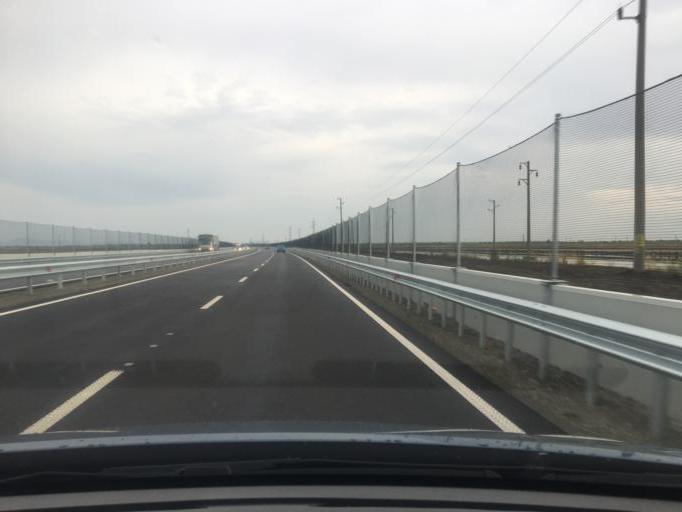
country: BG
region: Burgas
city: Aheloy
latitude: 42.6207
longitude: 27.6272
